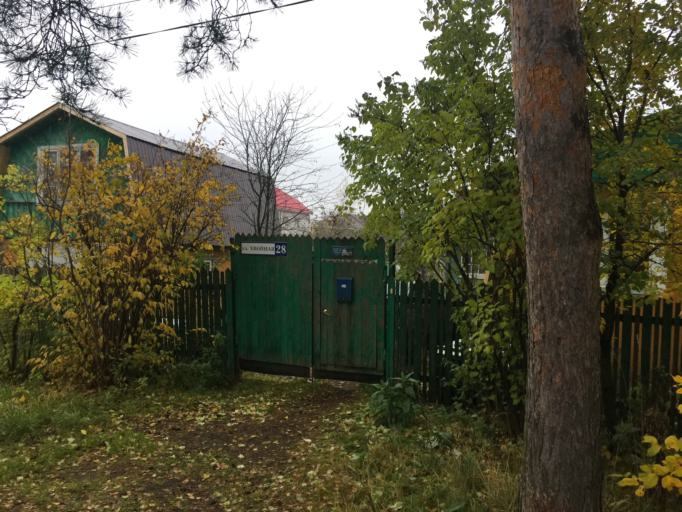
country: RU
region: Jaroslavl
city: Yaroslavl
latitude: 57.7243
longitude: 39.7695
